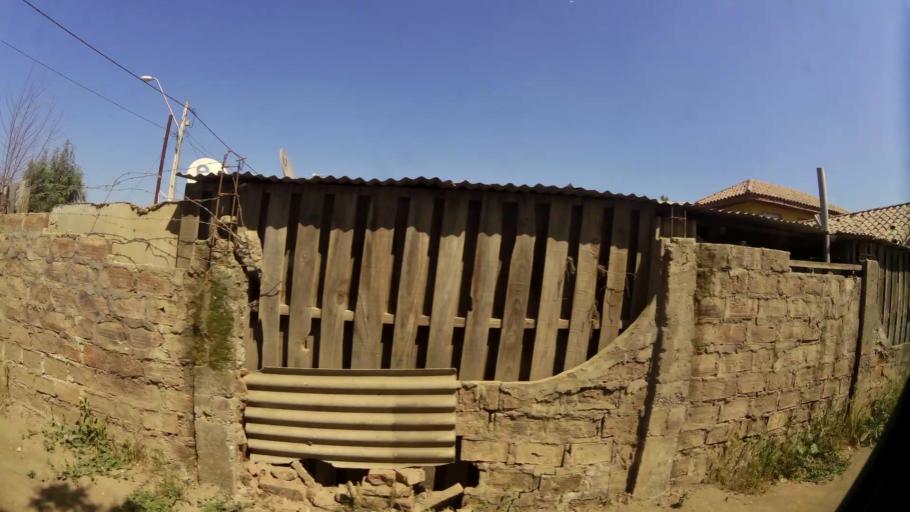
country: CL
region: Santiago Metropolitan
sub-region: Provincia de Talagante
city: Penaflor
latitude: -33.5831
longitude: -70.8132
